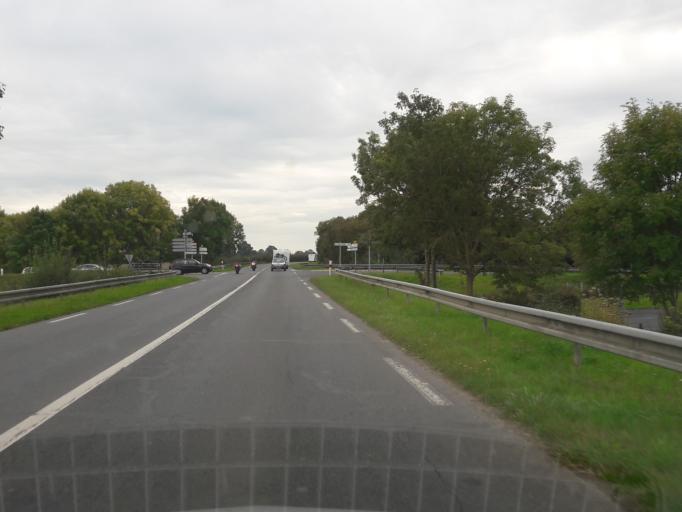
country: FR
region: Lower Normandy
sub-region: Departement du Calvados
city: Bayeux
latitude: 49.2674
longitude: -0.7095
